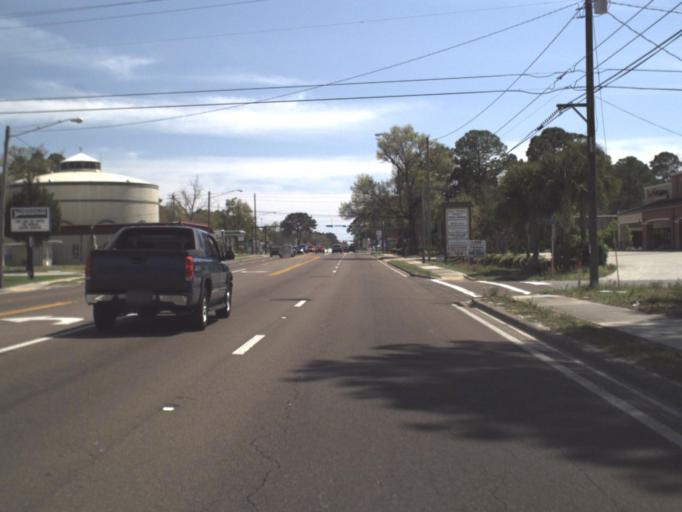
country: US
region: Florida
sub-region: Bay County
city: Lynn Haven
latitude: 30.2426
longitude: -85.6488
